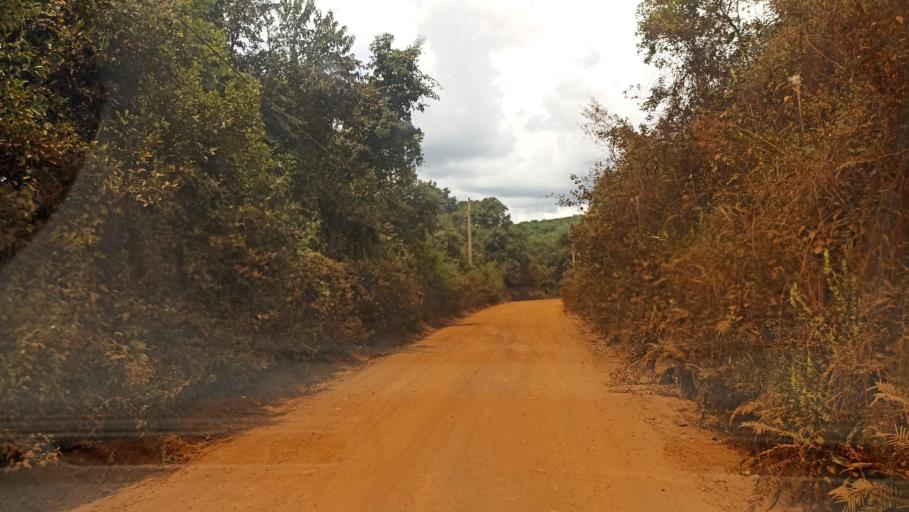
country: BR
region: Minas Gerais
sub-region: Itabirito
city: Itabirito
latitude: -20.3369
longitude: -43.7679
